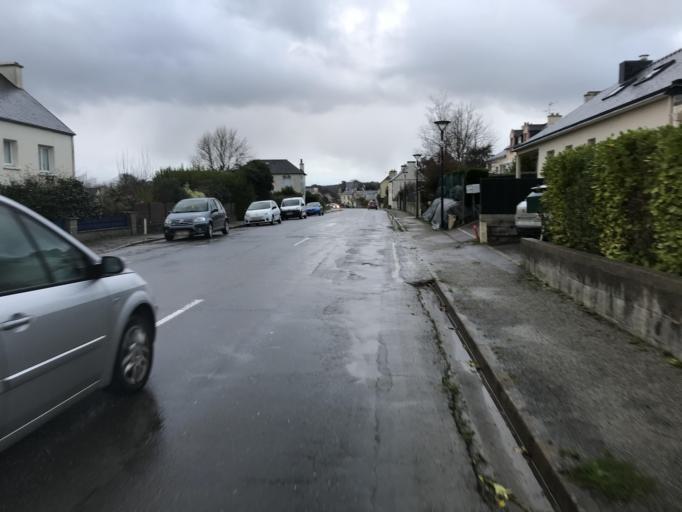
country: FR
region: Brittany
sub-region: Departement du Finistere
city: Loperhet
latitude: 48.3765
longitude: -4.3081
